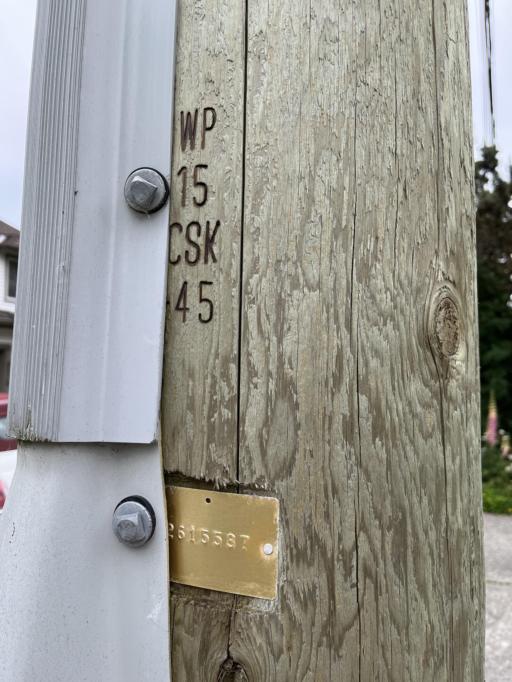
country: CA
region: British Columbia
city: Ladner
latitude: 49.0928
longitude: -123.0757
